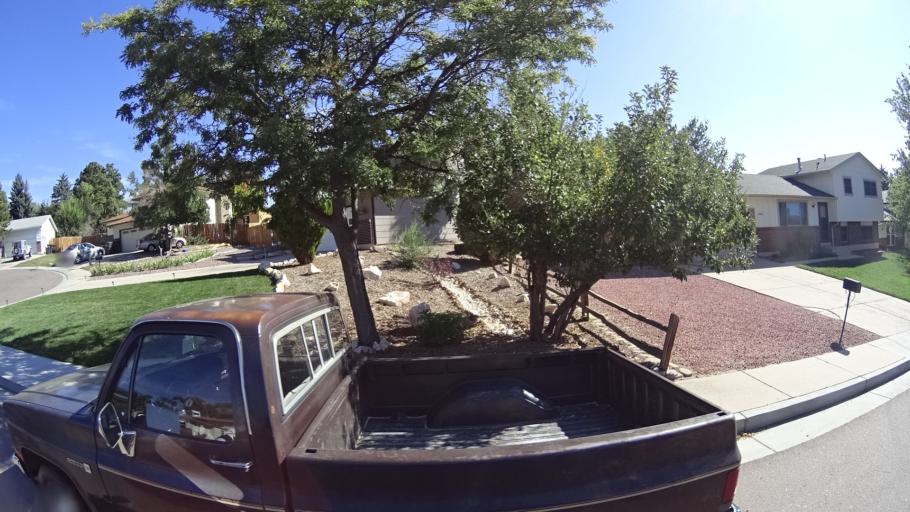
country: US
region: Colorado
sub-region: El Paso County
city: Colorado Springs
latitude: 38.9092
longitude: -104.7734
